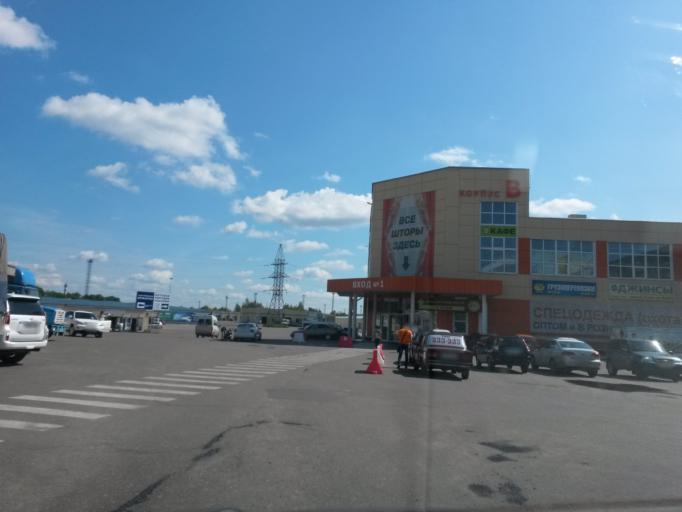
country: RU
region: Ivanovo
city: Bogorodskoye
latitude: 57.0105
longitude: 41.0093
